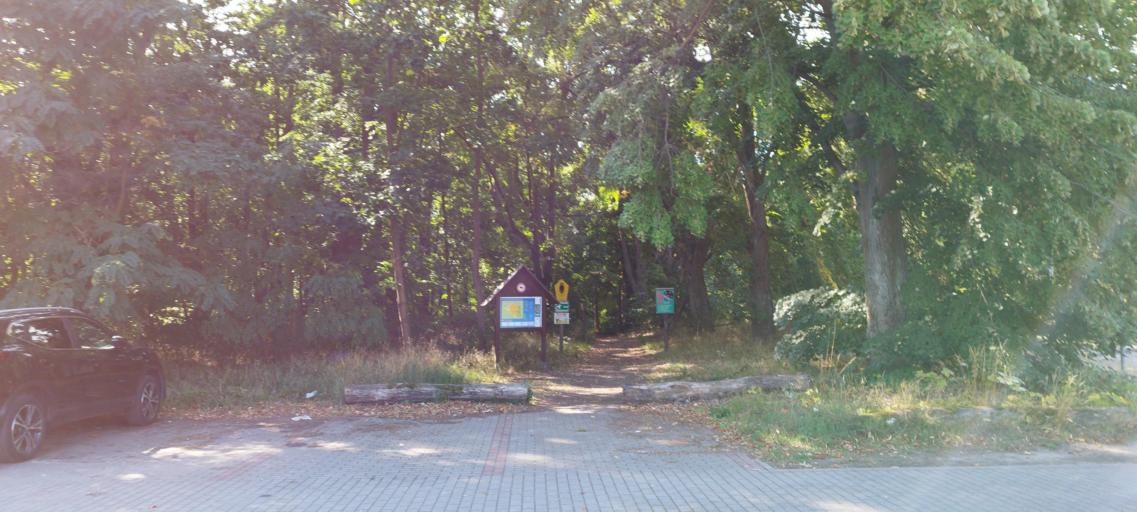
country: DE
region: Brandenburg
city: Dallgow-Doeberitz
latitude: 52.5336
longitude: 13.0556
